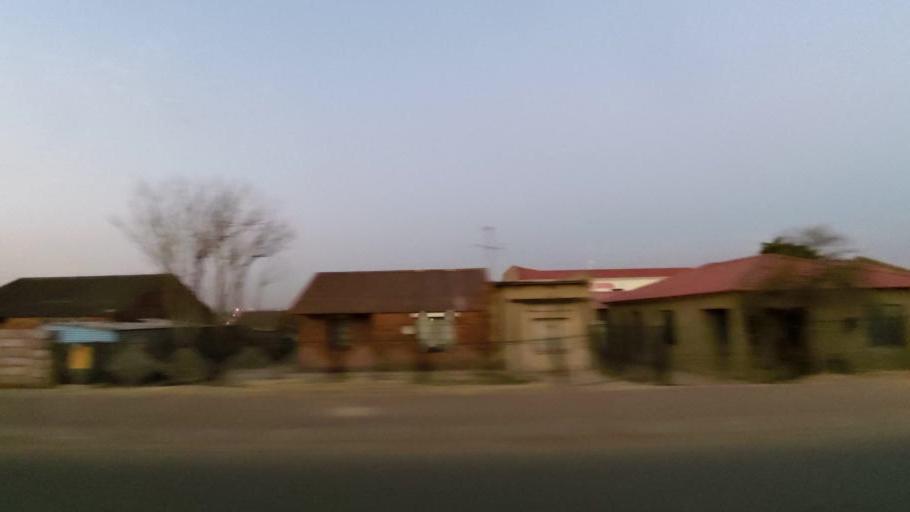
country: ZA
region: Gauteng
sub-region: City of Johannesburg Metropolitan Municipality
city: Soweto
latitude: -26.2333
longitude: 27.9122
